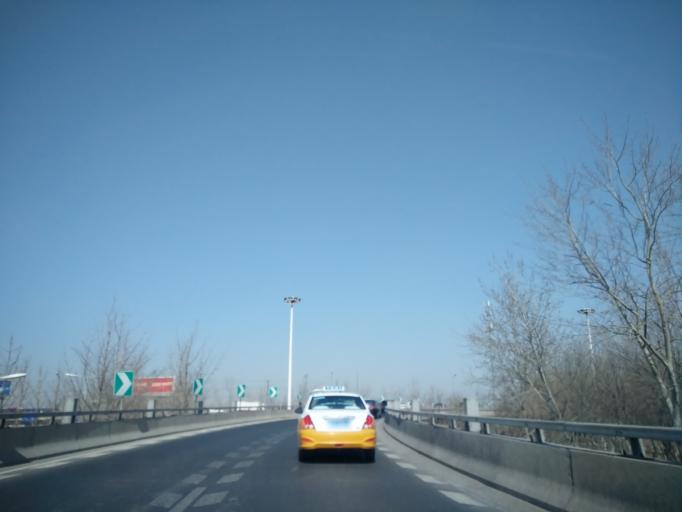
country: CN
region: Beijing
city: Jiugong
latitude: 39.8127
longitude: 116.4873
